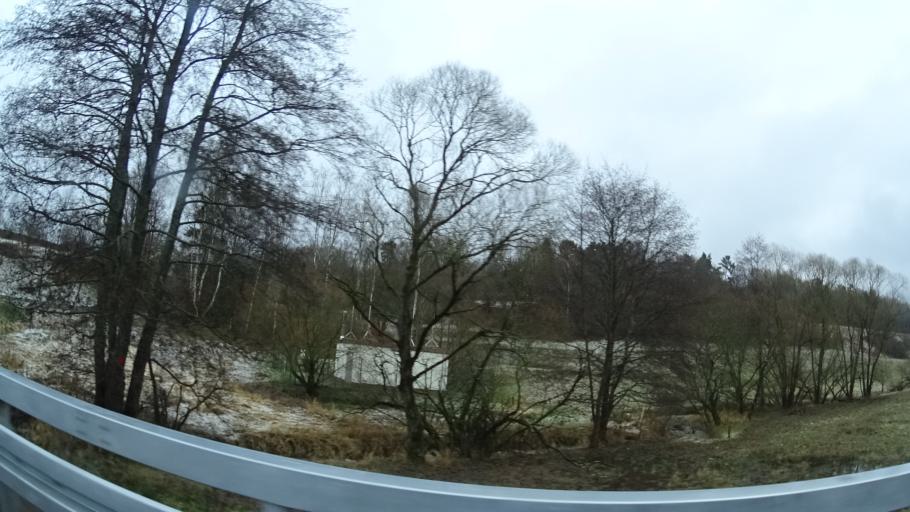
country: DE
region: Thuringia
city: Viernau
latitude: 50.6574
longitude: 10.5678
